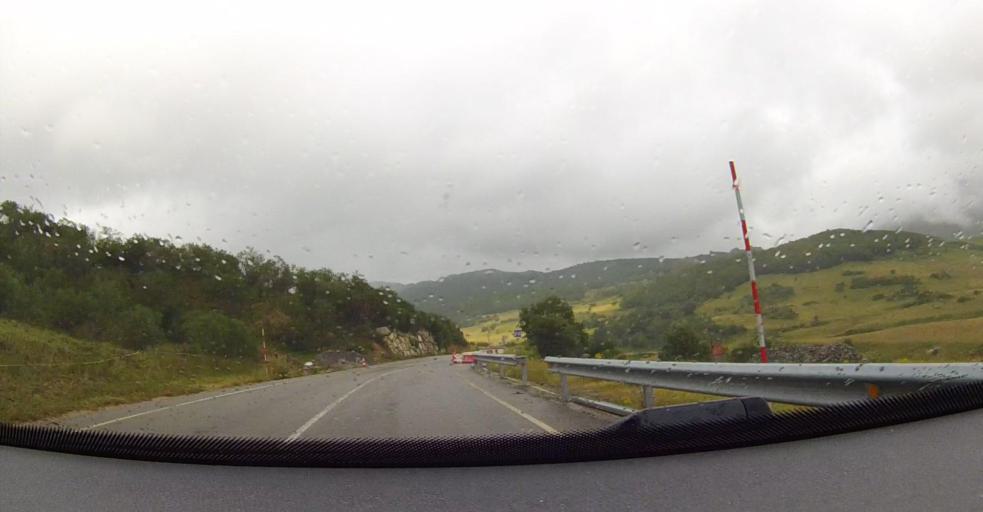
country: ES
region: Castille and Leon
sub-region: Provincia de Leon
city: Marana
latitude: 43.0718
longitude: -5.2030
